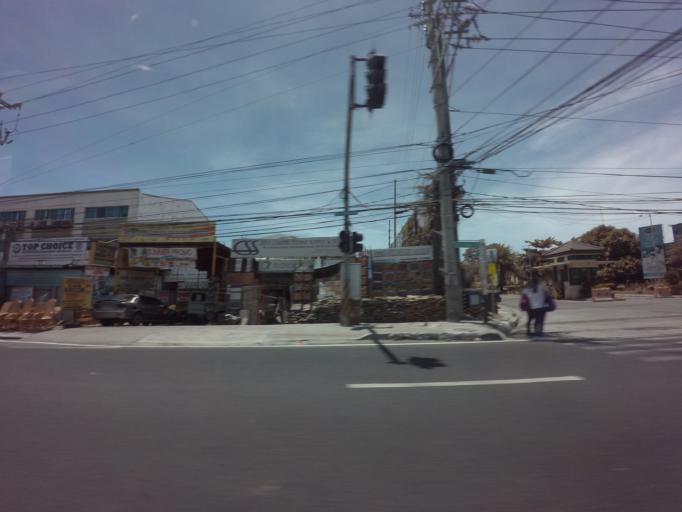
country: PH
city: Sambayanihan People's Village
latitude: 14.4885
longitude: 120.9915
